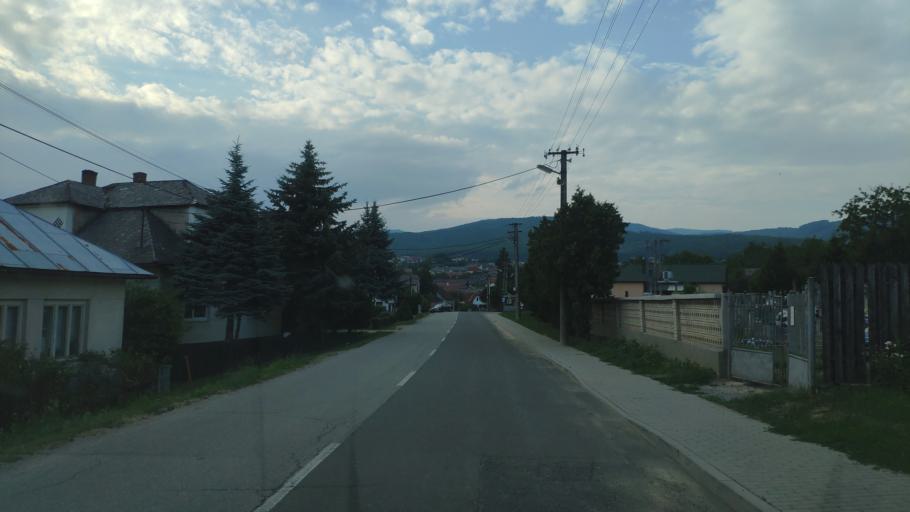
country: SK
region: Kosicky
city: Medzev
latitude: 48.7061
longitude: 20.9752
